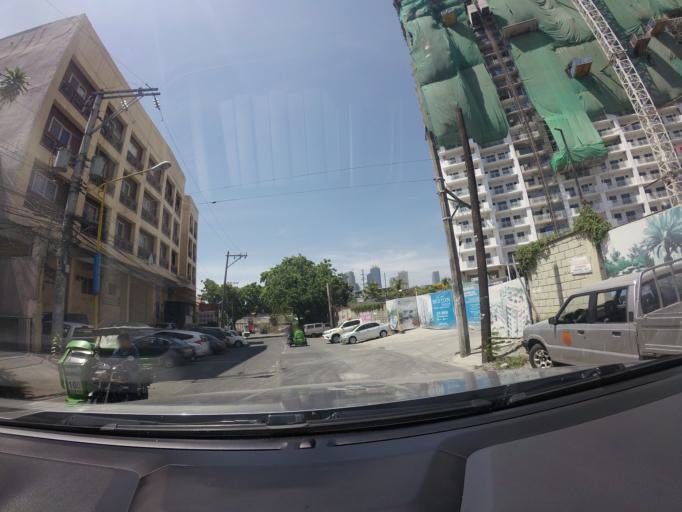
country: PH
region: Metro Manila
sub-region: Pasig
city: Pasig City
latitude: 14.5693
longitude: 121.0557
